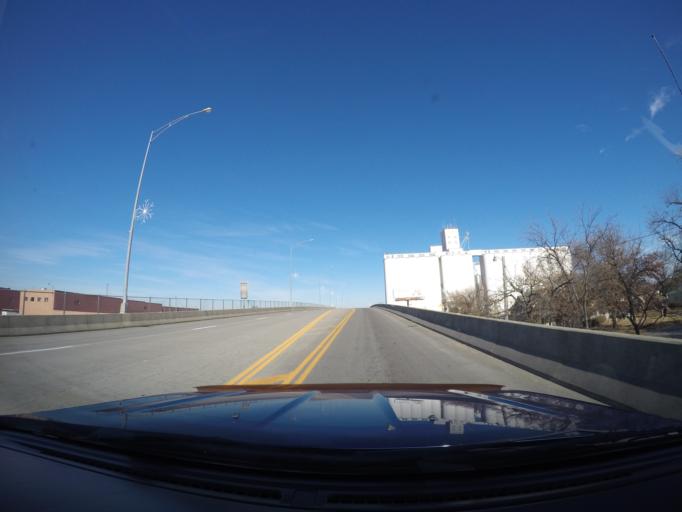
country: US
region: Kansas
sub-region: Cloud County
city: Concordia
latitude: 39.5723
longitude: -97.6575
